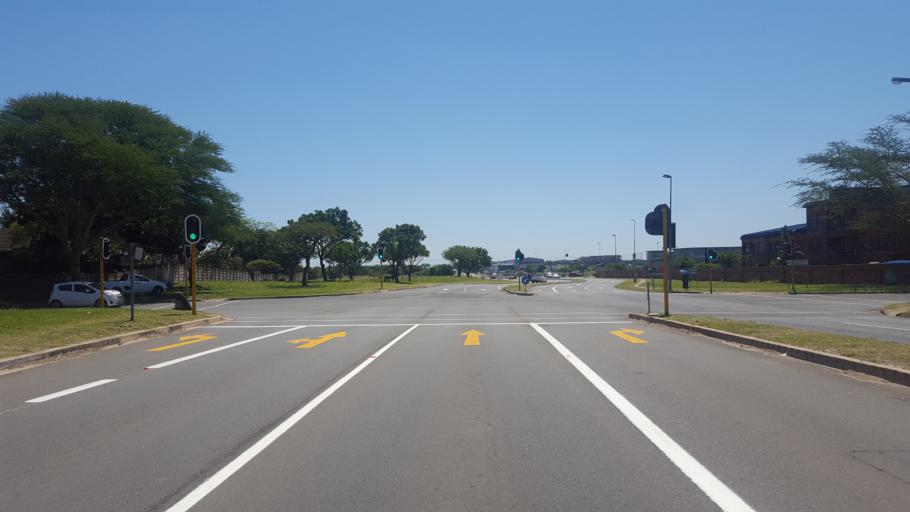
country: ZA
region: KwaZulu-Natal
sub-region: uThungulu District Municipality
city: Richards Bay
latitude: -28.7607
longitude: 32.0531
